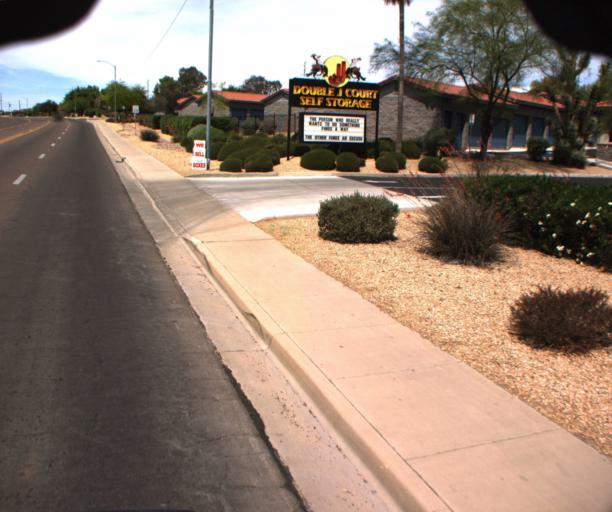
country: US
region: Arizona
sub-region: Maricopa County
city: Wickenburg
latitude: 33.9661
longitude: -112.7372
